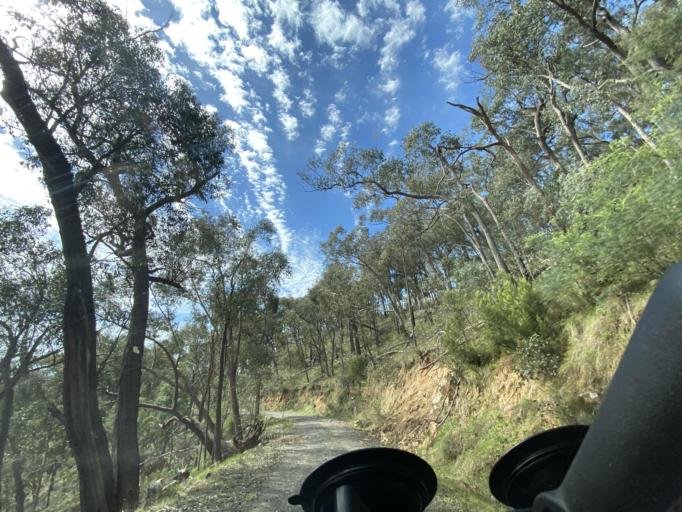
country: AU
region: Victoria
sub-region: Mansfield
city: Mansfield
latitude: -36.8100
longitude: 146.1031
